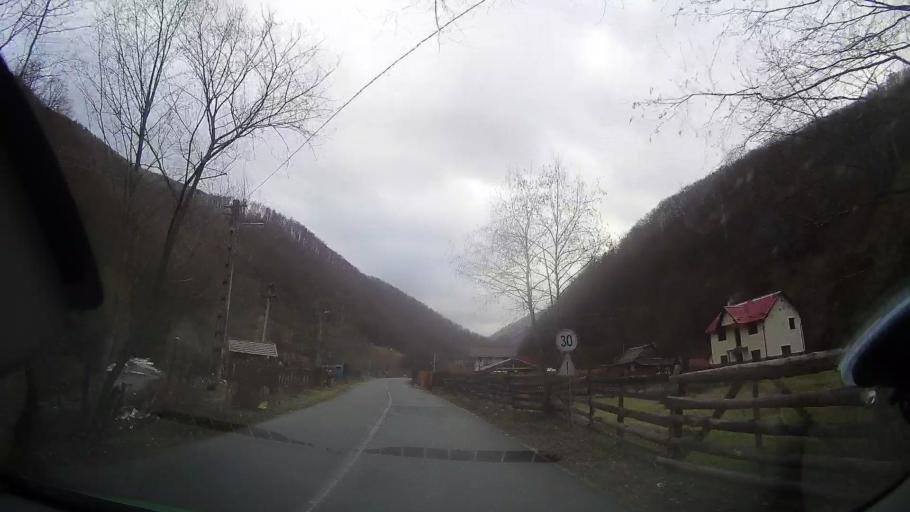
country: RO
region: Cluj
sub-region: Comuna Maguri-Racatau
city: Maguri-Racatau
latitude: 46.6583
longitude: 23.2155
